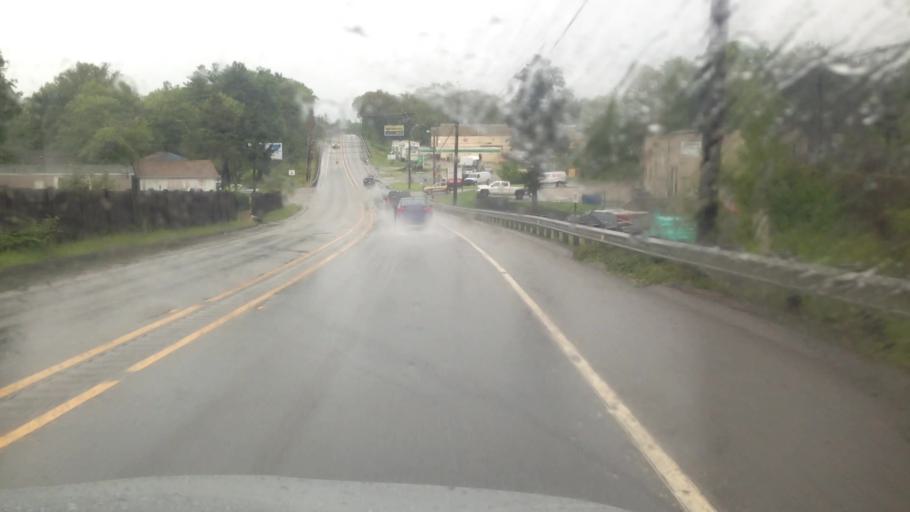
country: US
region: Massachusetts
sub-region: Worcester County
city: Auburn
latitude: 42.1889
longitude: -71.8291
